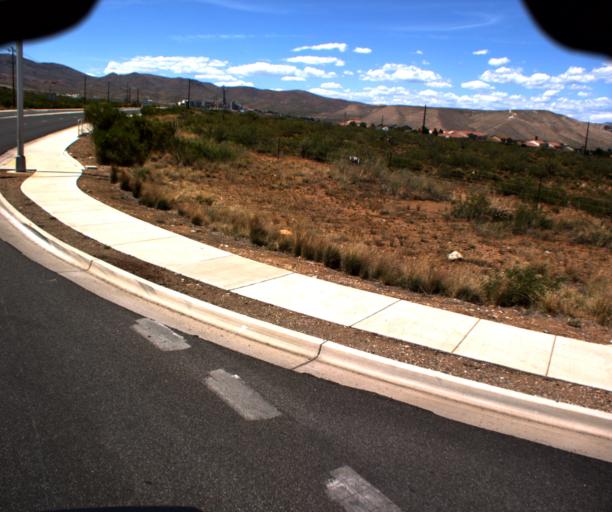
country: US
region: Arizona
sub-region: Yavapai County
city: Clarkdale
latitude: 34.7587
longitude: -112.0587
